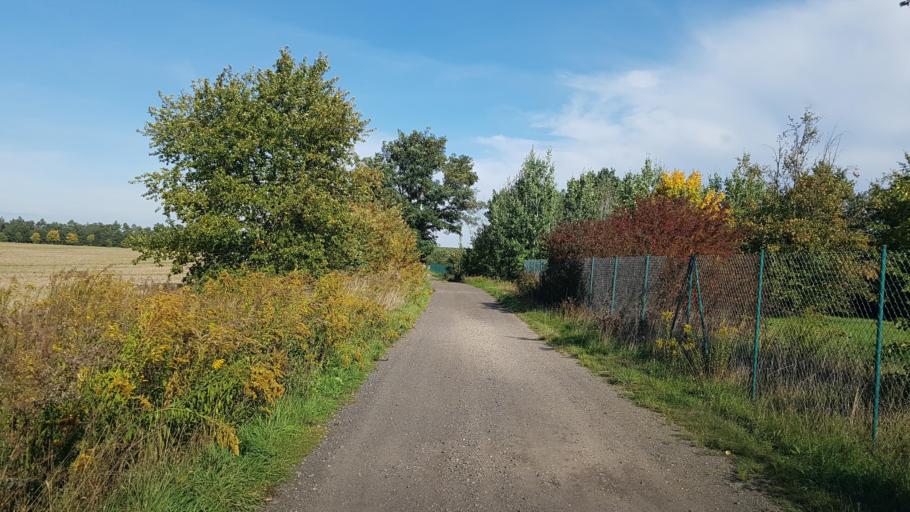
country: DE
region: Brandenburg
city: Belzig
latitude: 52.1486
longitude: 12.6087
